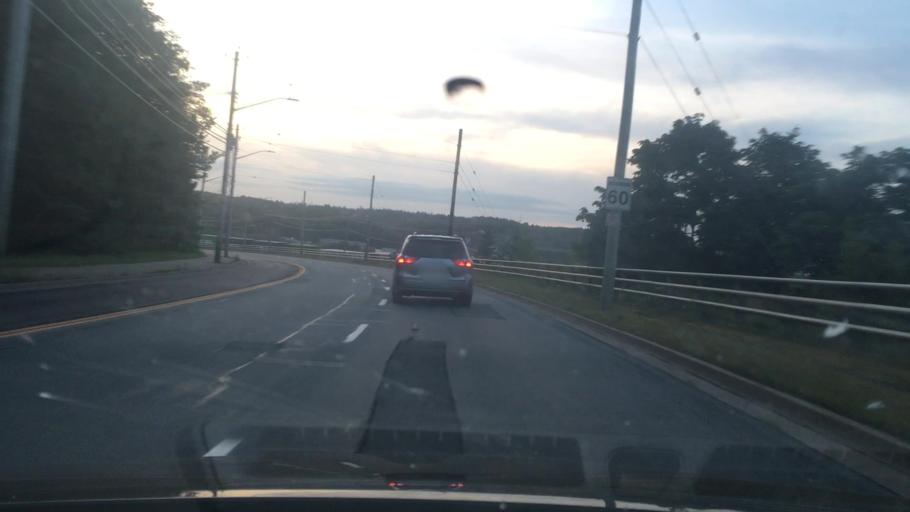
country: CA
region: Nova Scotia
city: Dartmouth
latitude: 44.6793
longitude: -63.6512
